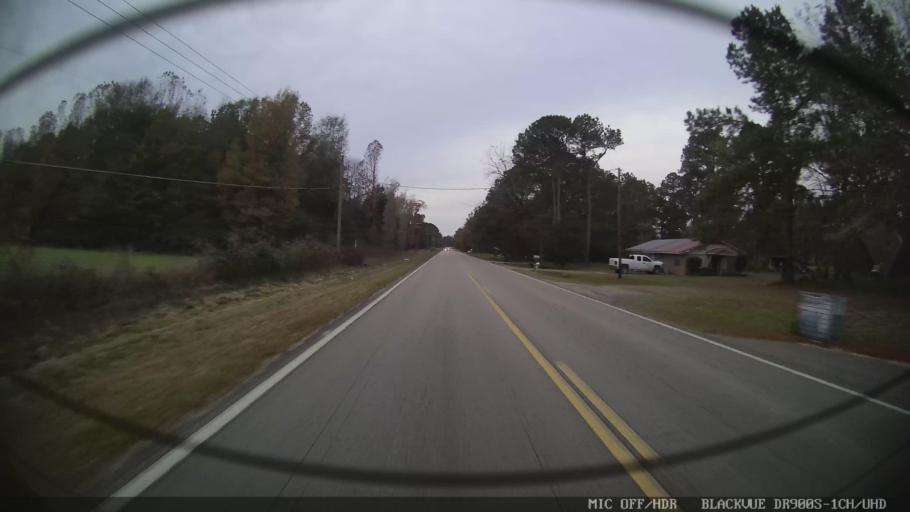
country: US
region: Mississippi
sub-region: Clarke County
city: Stonewall
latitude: 32.0249
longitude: -88.8558
